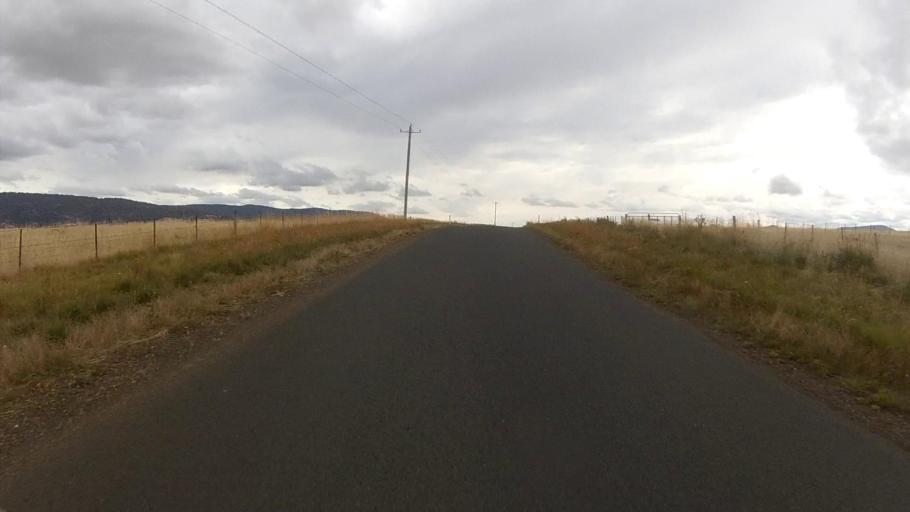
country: AU
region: Tasmania
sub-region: Northern Midlands
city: Evandale
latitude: -41.8277
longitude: 147.7849
